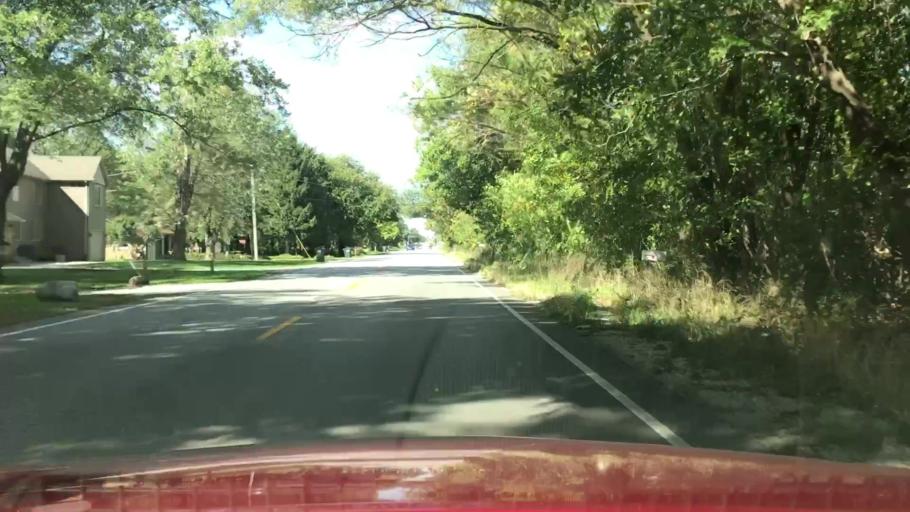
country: US
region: Illinois
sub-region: Cook County
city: Lynwood
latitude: 41.5212
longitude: -87.5526
